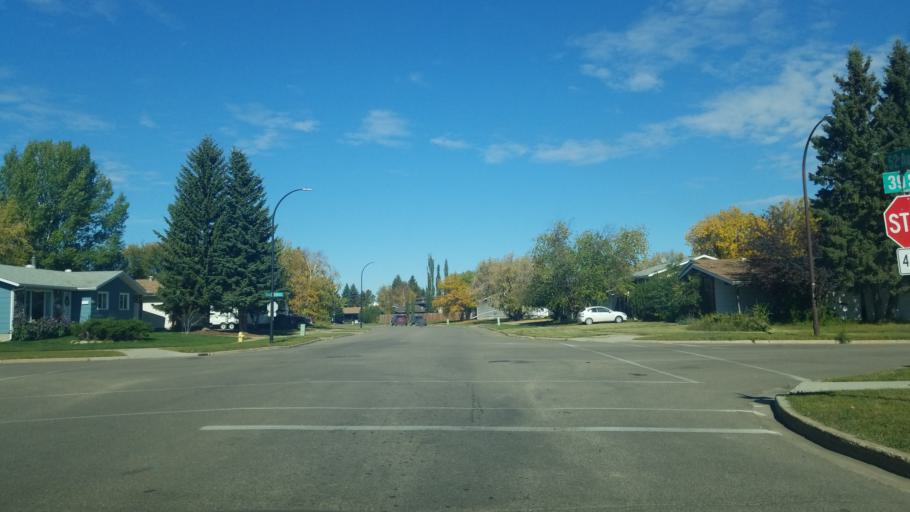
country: CA
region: Saskatchewan
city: Lloydminster
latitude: 53.2730
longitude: -110.0123
